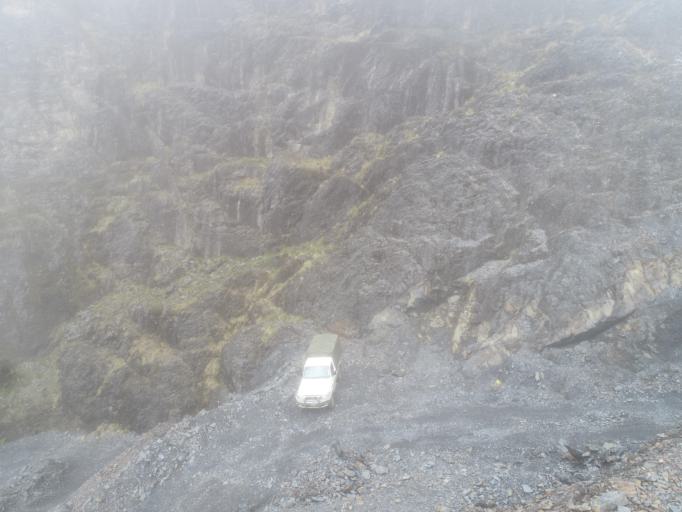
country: PE
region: Puno
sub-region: San Antonio De Putina
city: Sina
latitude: -14.7369
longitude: -69.0501
